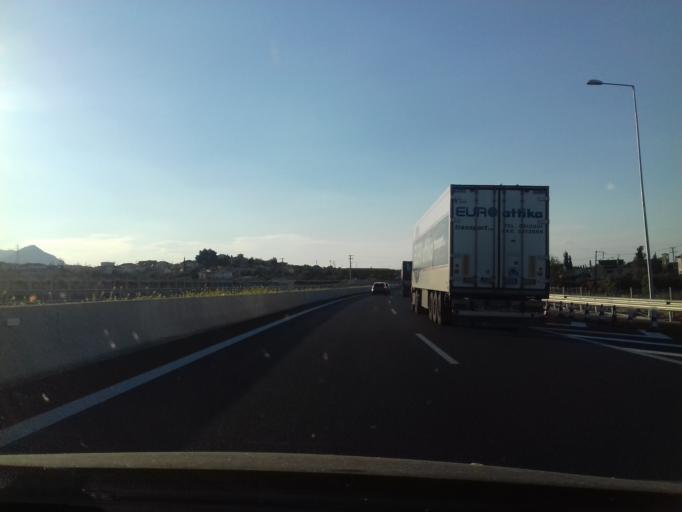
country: GR
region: Peloponnese
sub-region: Nomos Korinthias
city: Xylokastro
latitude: 38.0587
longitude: 22.6589
